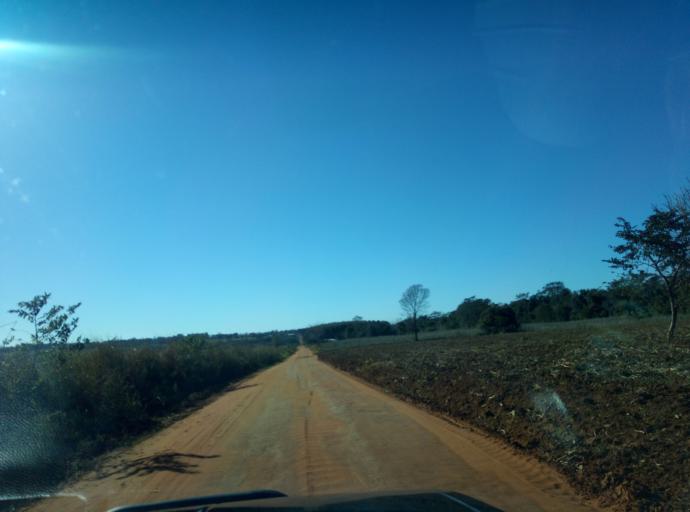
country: PY
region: Caaguazu
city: Doctor Cecilio Baez
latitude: -25.1624
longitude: -56.2673
